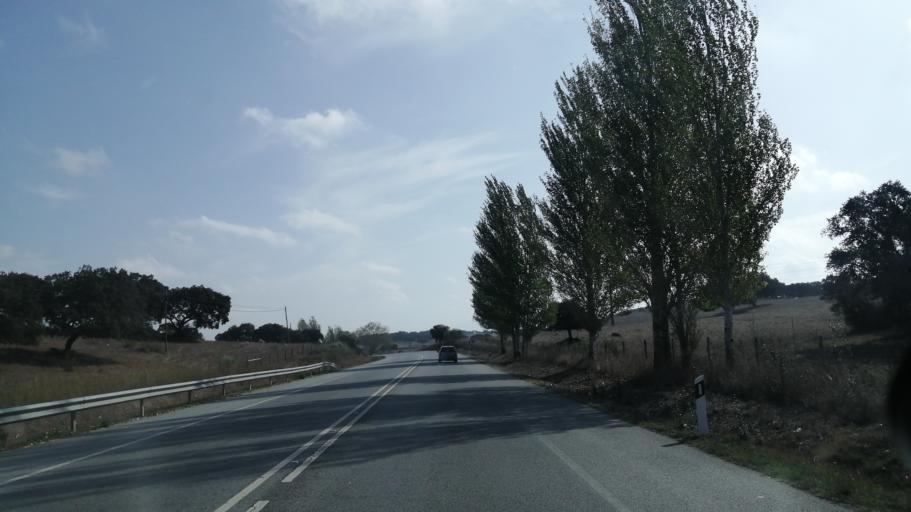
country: PT
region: Evora
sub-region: Montemor-O-Novo
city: Montemor-o-Novo
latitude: 38.6442
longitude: -8.1828
